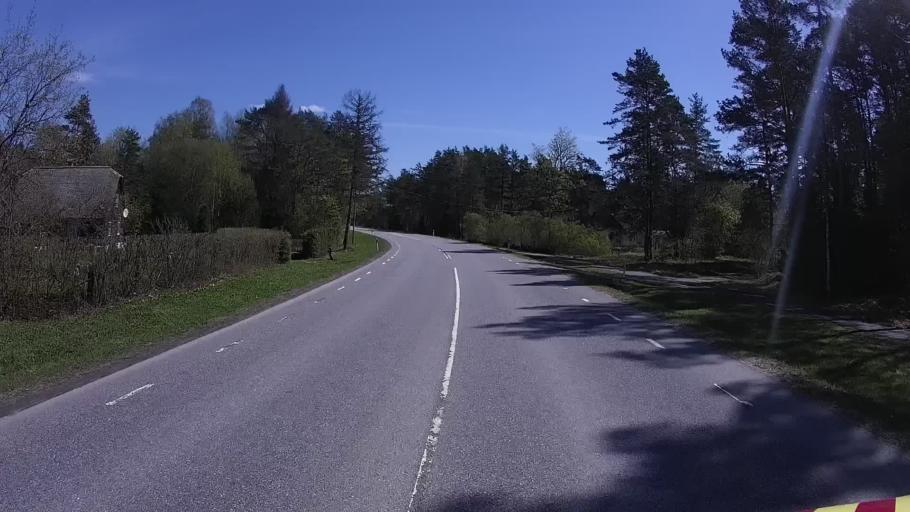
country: EE
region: Harju
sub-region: Nissi vald
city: Turba
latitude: 59.2263
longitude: 24.1504
